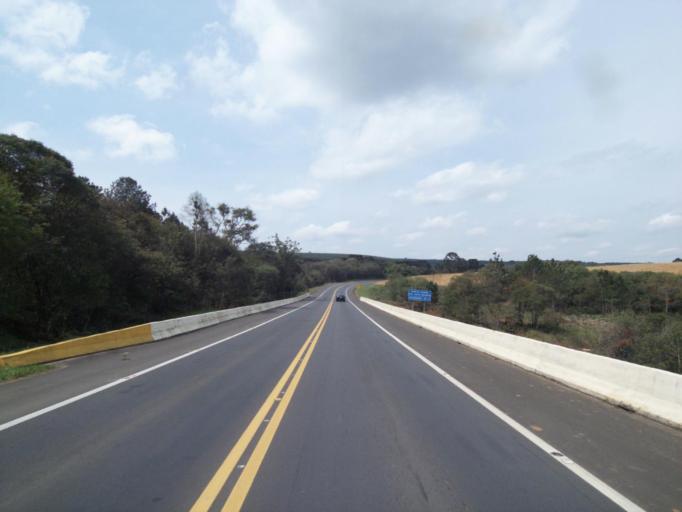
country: BR
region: Parana
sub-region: Irati
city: Irati
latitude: -25.4538
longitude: -50.4553
